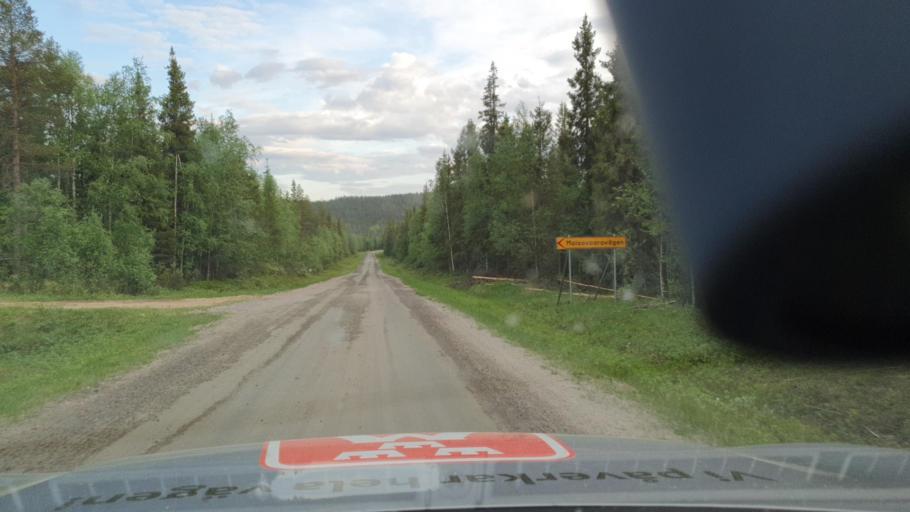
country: SE
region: Norrbotten
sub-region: Bodens Kommun
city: Boden
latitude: 66.6111
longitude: 21.3537
